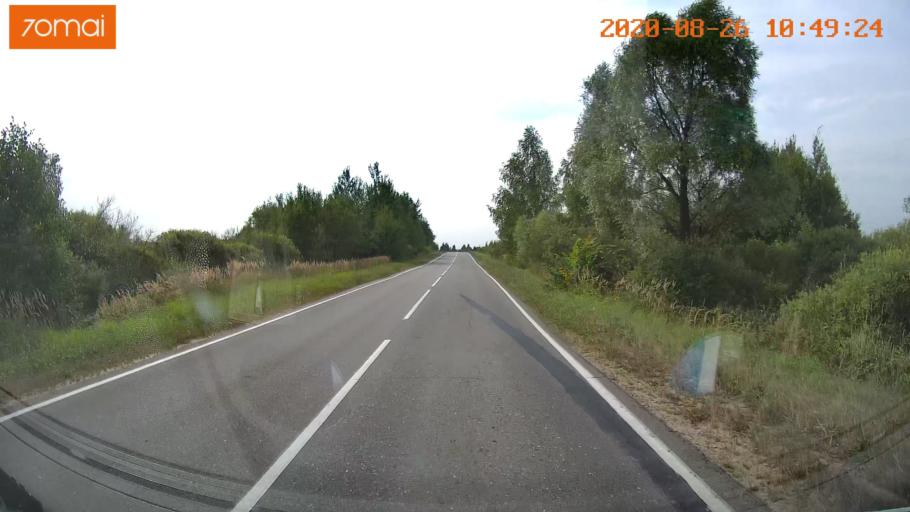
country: RU
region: Rjazan
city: Lashma
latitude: 54.7030
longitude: 41.1603
